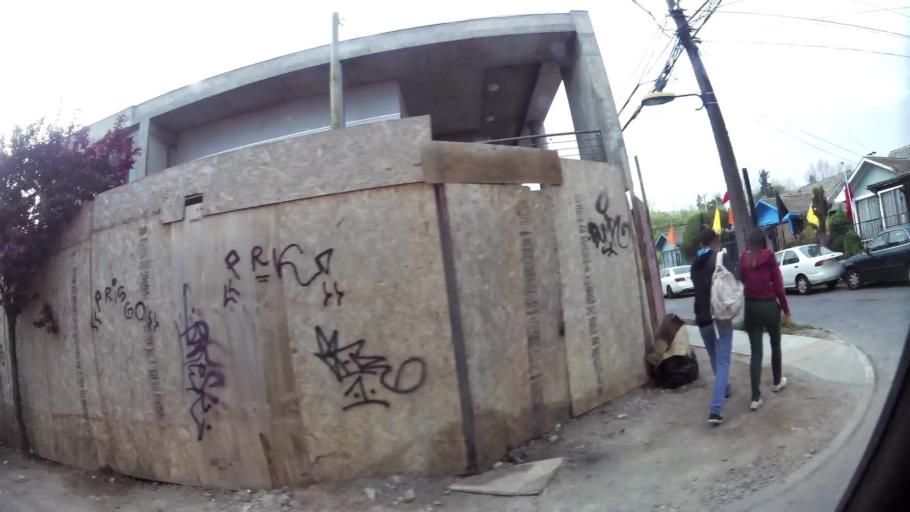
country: CL
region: Santiago Metropolitan
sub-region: Provincia de Santiago
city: Lo Prado
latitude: -33.5112
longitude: -70.7547
